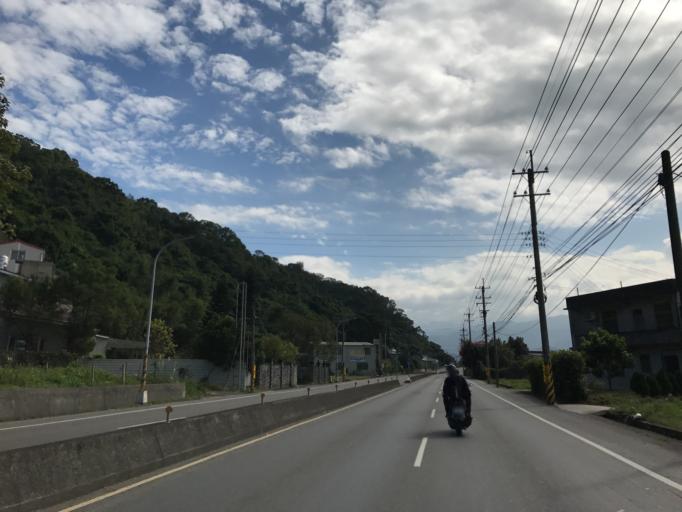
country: TW
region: Taiwan
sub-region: Hsinchu
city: Zhubei
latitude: 24.7419
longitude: 121.1079
